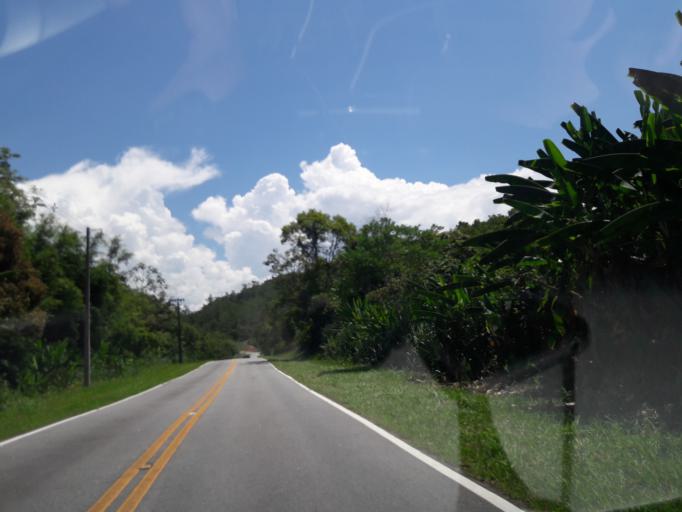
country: BR
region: Parana
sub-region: Antonina
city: Antonina
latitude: -25.5240
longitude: -48.7660
